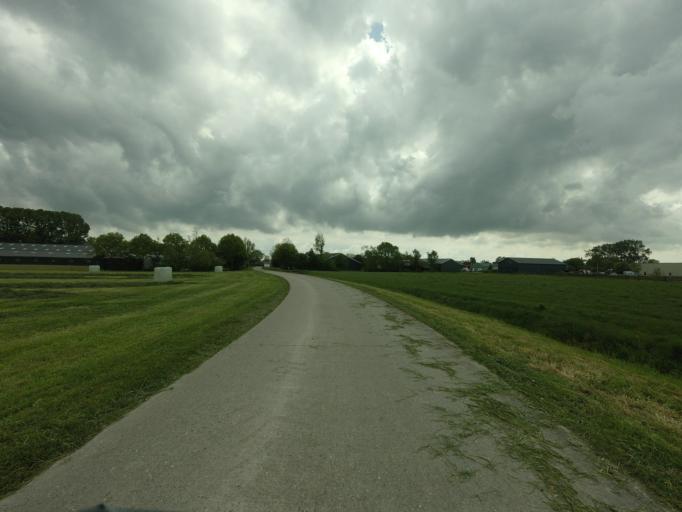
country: NL
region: Friesland
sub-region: Gemeente Littenseradiel
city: Wommels
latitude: 53.1042
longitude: 5.6228
